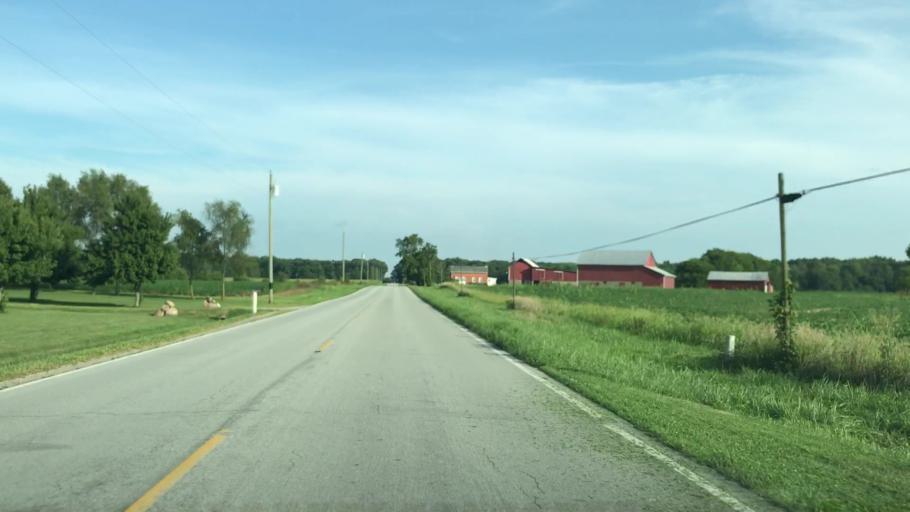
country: US
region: Ohio
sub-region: Union County
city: Marysville
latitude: 40.1994
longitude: -83.3435
